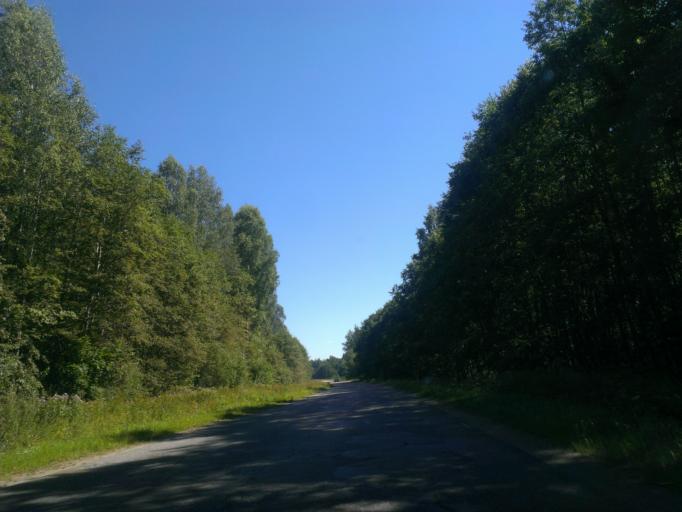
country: LV
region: Incukalns
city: Incukalns
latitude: 57.0243
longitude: 24.7541
